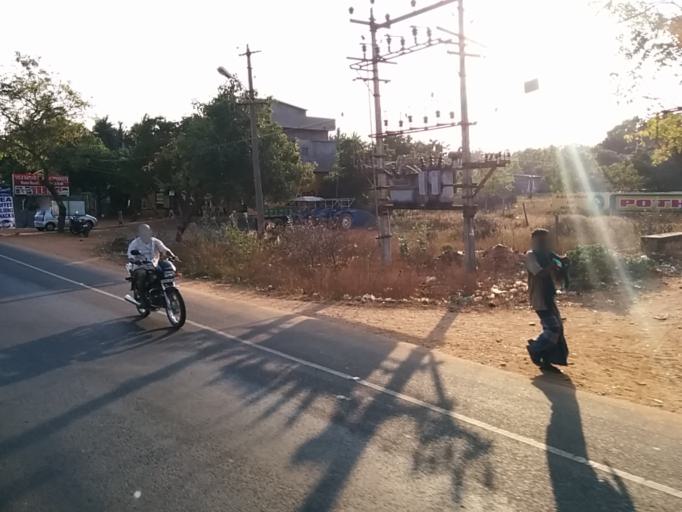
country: IN
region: Tamil Nadu
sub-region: Villupuram
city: Auroville
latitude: 12.0041
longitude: 79.8543
